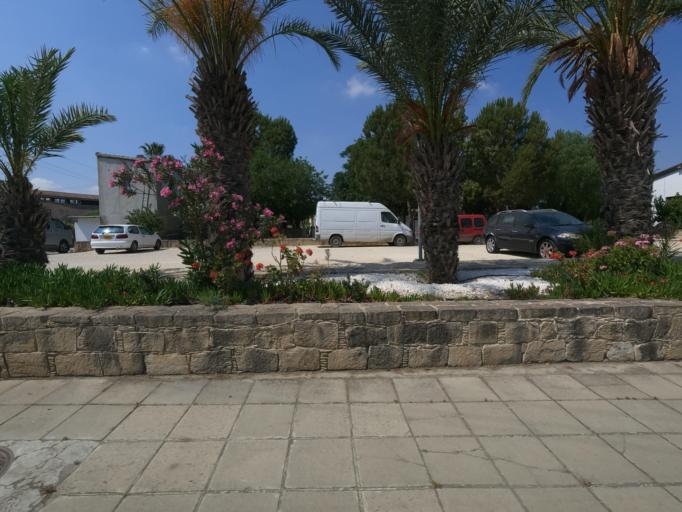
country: CY
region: Lefkosia
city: Dali
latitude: 35.0433
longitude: 33.4453
